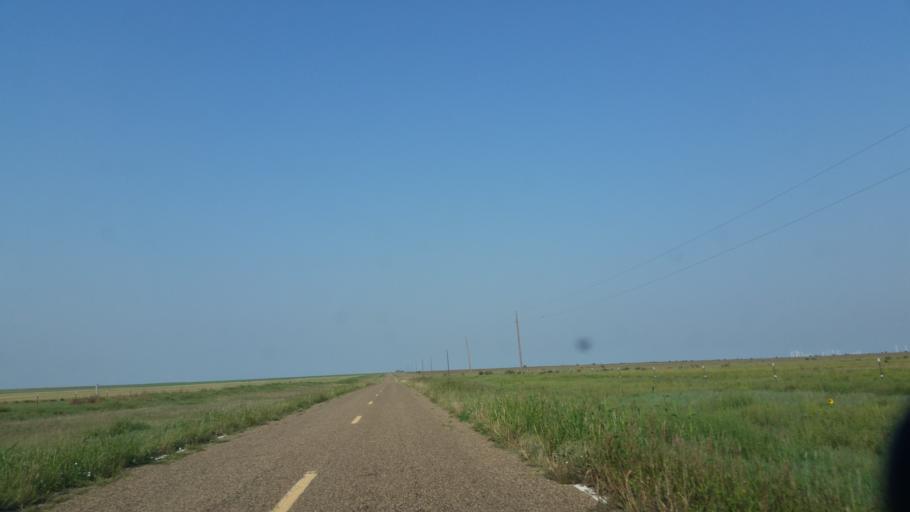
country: US
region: New Mexico
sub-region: Quay County
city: Logan
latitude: 34.9230
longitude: -103.2466
